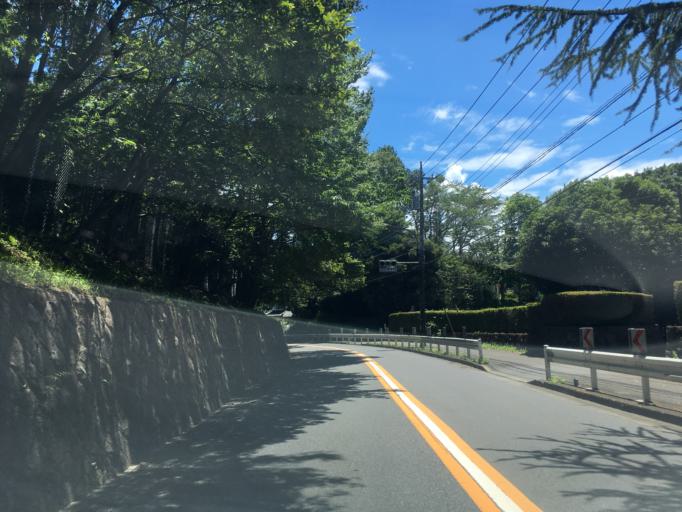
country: JP
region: Tokyo
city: Kokubunji
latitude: 35.6360
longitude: 139.4639
